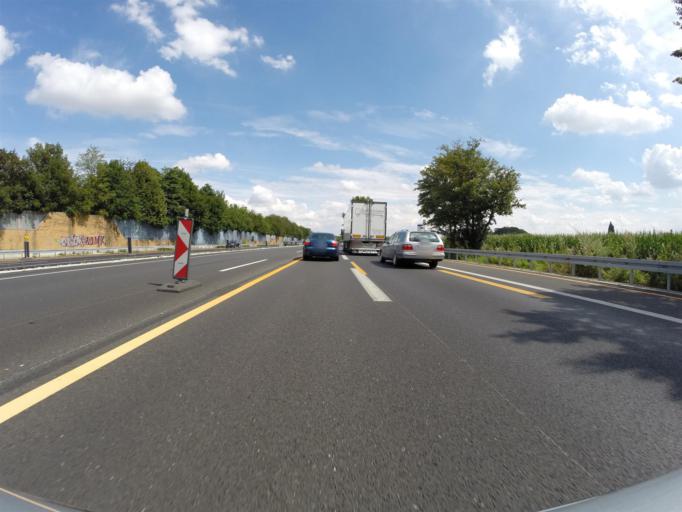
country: DE
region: North Rhine-Westphalia
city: Buende
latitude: 52.1927
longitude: 8.5651
